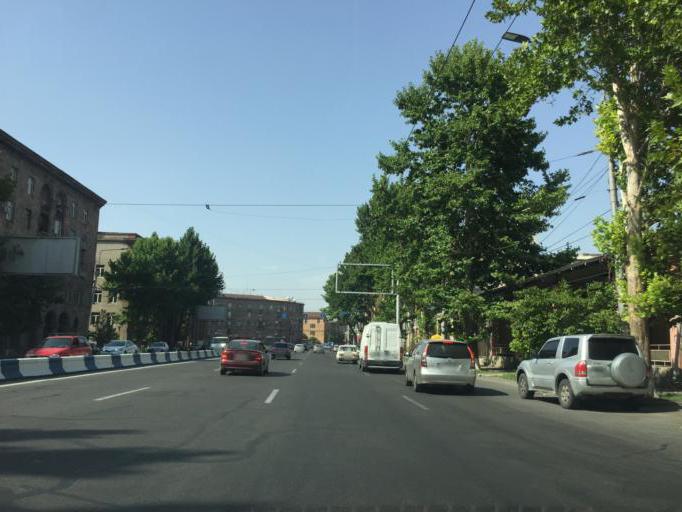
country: AM
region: Yerevan
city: Yerevan
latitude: 40.1503
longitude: 44.4981
